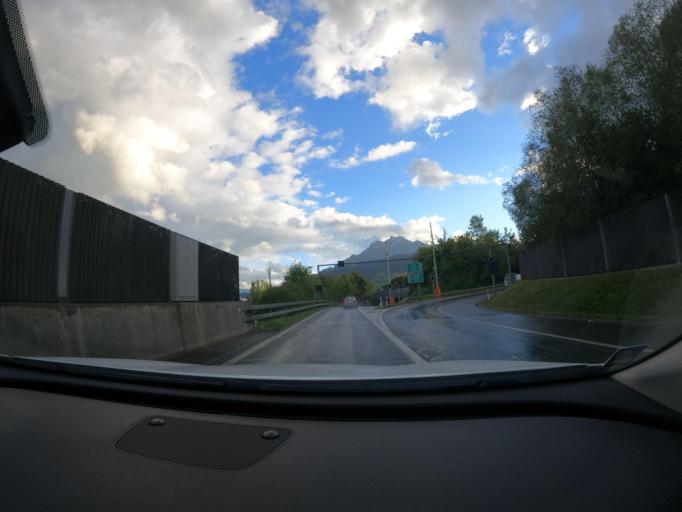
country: CH
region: Lucerne
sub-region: Lucerne-Stadt District
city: Luzern
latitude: 47.0377
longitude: 8.2967
